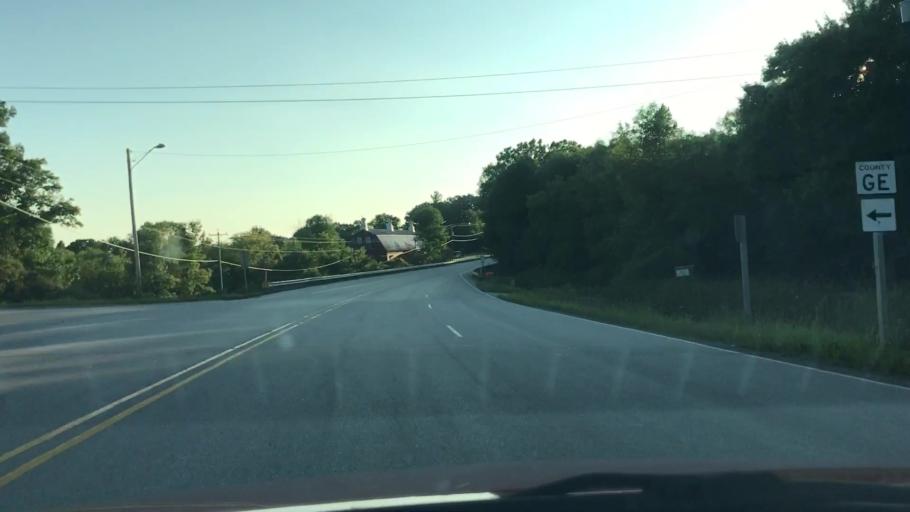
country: US
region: Wisconsin
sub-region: Brown County
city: Oneida
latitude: 44.5121
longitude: -88.1500
